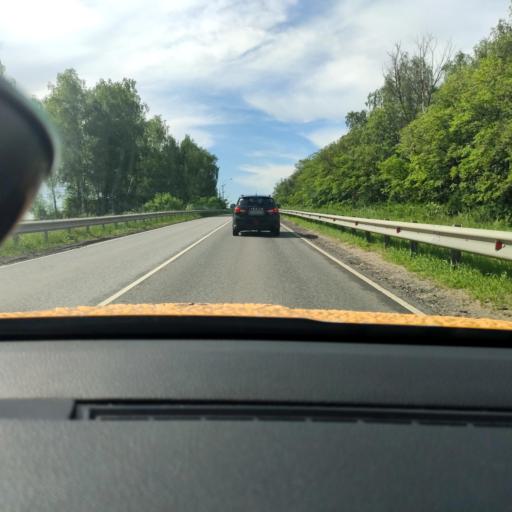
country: RU
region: Moskovskaya
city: Stupino
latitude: 54.9393
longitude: 38.0374
